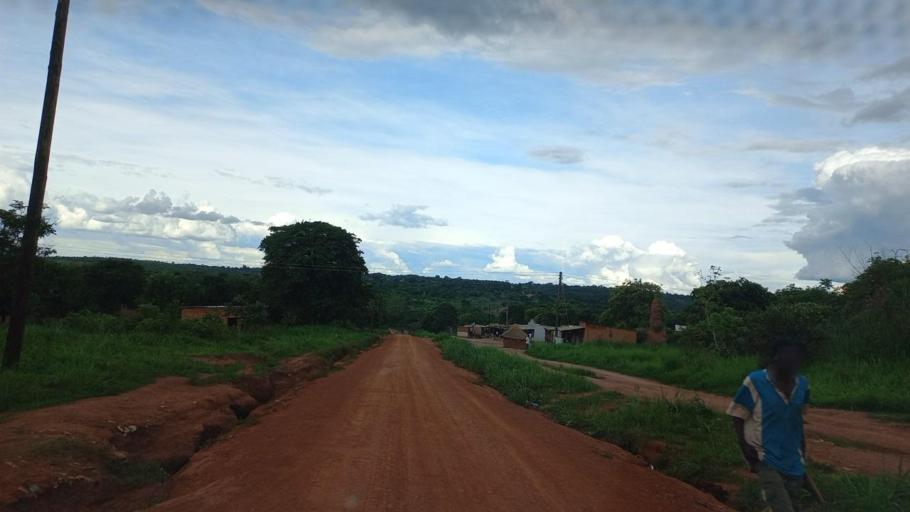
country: ZM
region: North-Western
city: Mwinilunga
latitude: -11.7560
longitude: 24.4336
